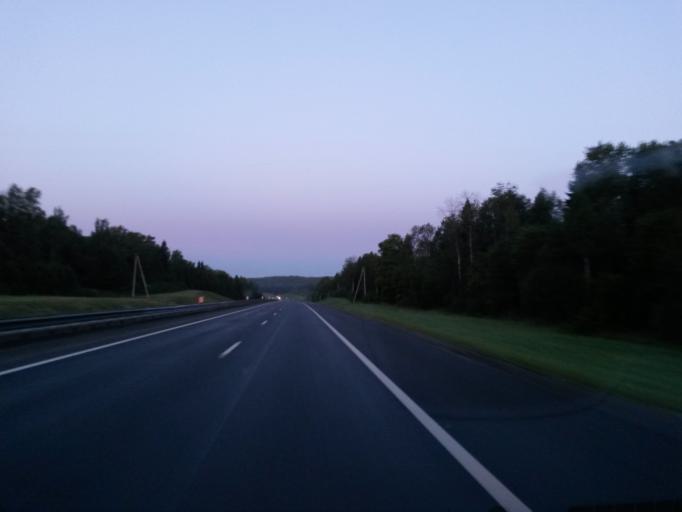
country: RU
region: Vladimir
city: Arsaki
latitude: 56.4895
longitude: 38.4323
